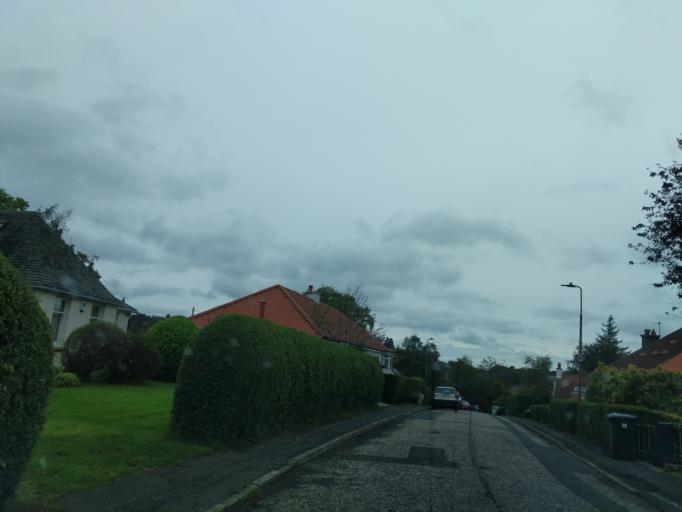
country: GB
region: Scotland
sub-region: Edinburgh
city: Balerno
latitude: 55.8831
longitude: -3.3424
